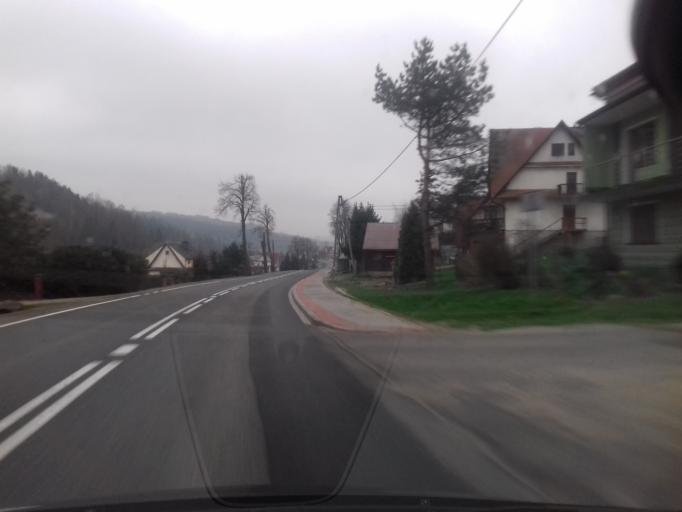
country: PL
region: Lesser Poland Voivodeship
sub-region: Powiat limanowski
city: Kasina Wielka
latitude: 49.6942
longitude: 20.1205
